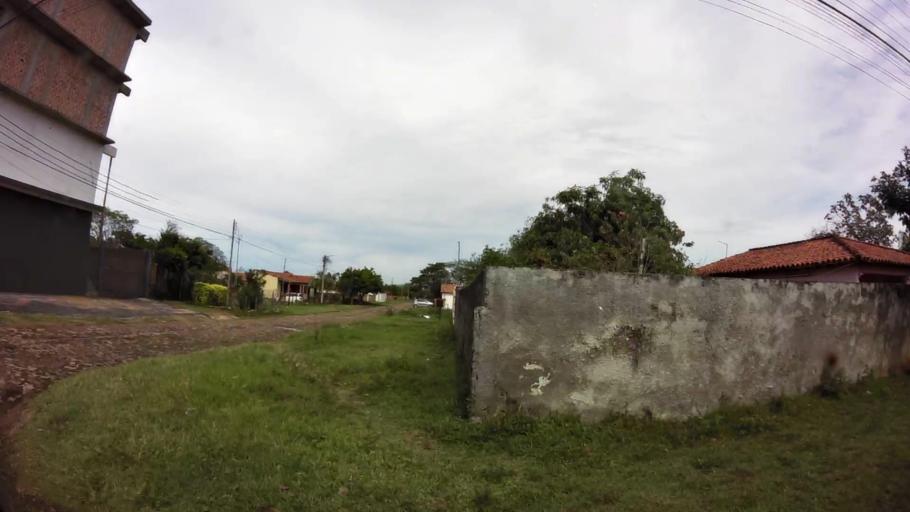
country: PY
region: Central
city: Limpio
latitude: -25.1647
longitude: -57.4787
